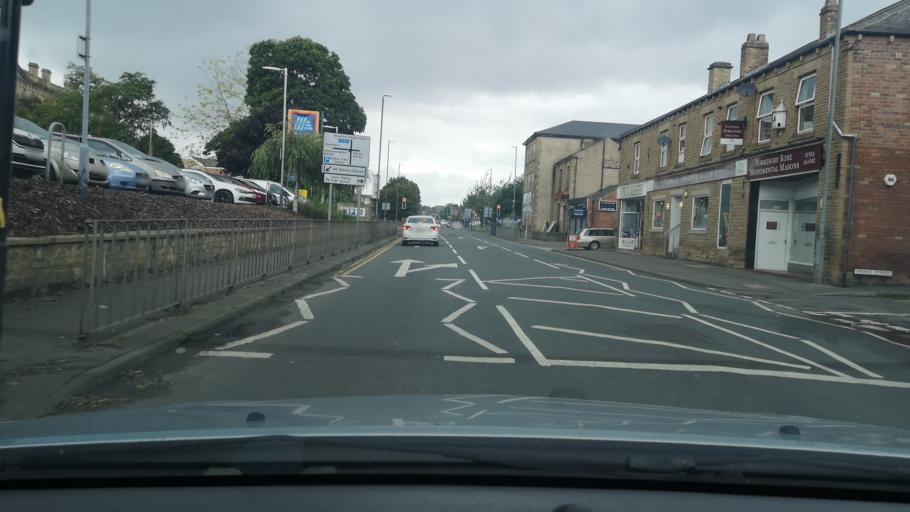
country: GB
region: England
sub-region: Kirklees
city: Batley
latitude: 53.7166
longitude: -1.6336
